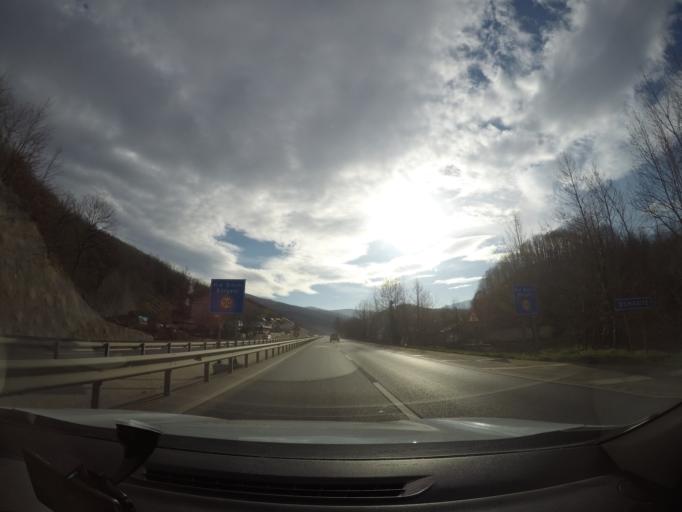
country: TR
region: Bursa
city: Tahtakopru
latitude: 39.9524
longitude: 29.6912
